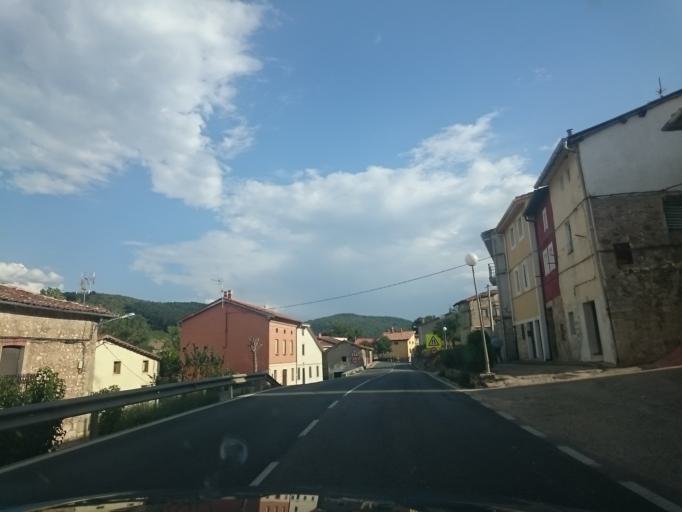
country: ES
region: Castille and Leon
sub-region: Provincia de Burgos
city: Espinosa del Camino
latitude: 42.3861
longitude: -3.3090
